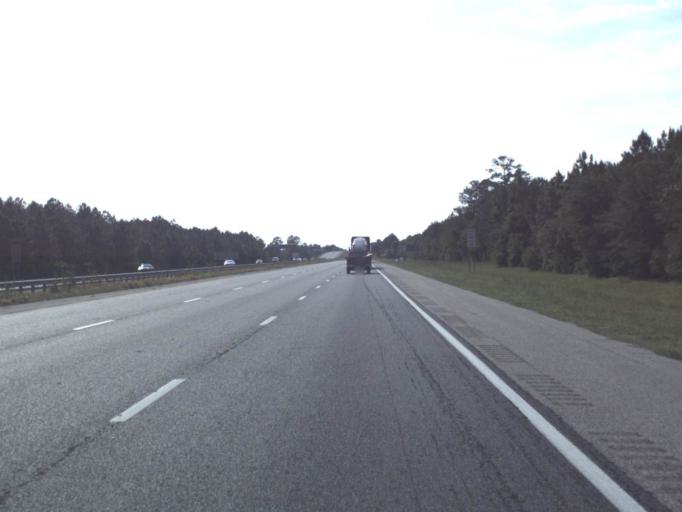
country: US
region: Florida
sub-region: Flagler County
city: Palm Coast
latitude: 29.6668
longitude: -81.2950
